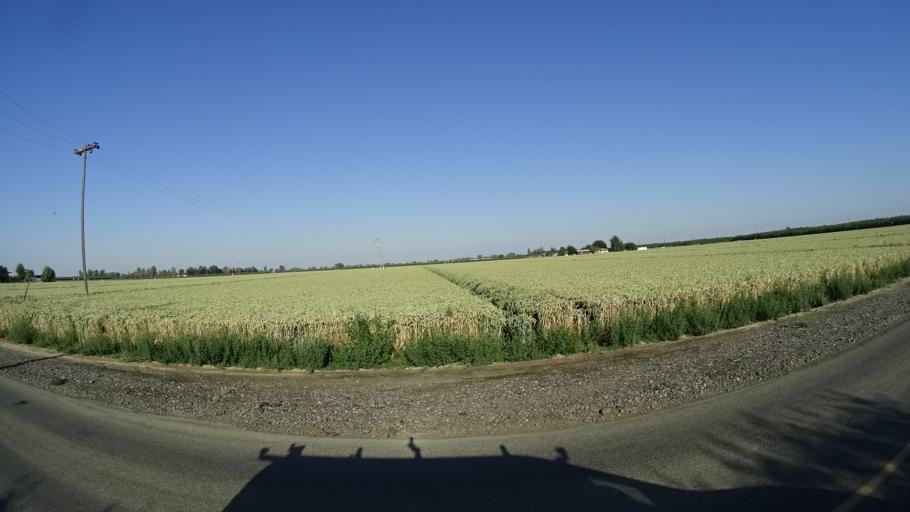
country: US
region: California
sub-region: Kings County
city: Lemoore
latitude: 36.2816
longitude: -119.7447
